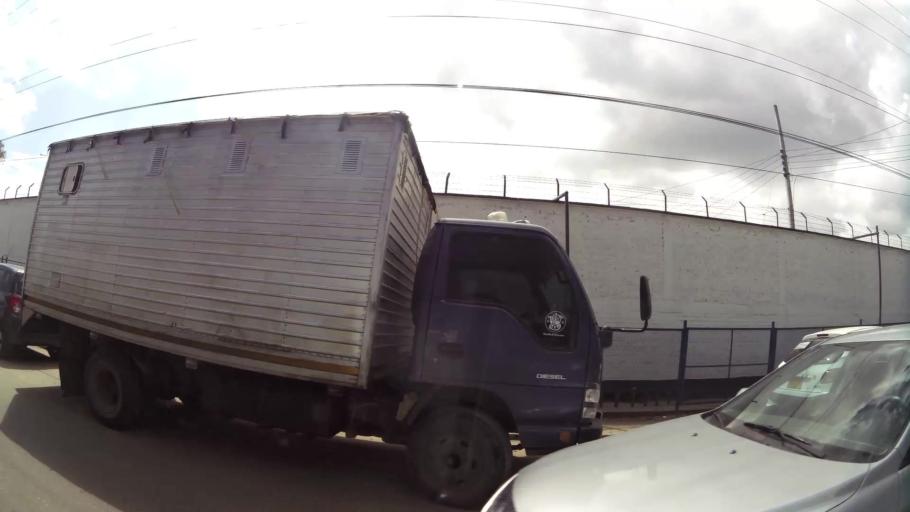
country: CO
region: Bogota D.C.
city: Bogota
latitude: 4.6350
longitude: -74.1063
